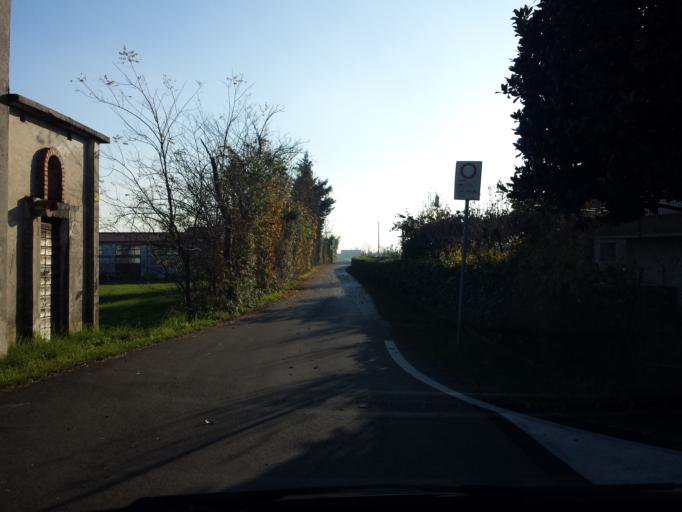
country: IT
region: Veneto
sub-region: Provincia di Vicenza
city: Sandrigo
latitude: 45.6817
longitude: 11.5842
